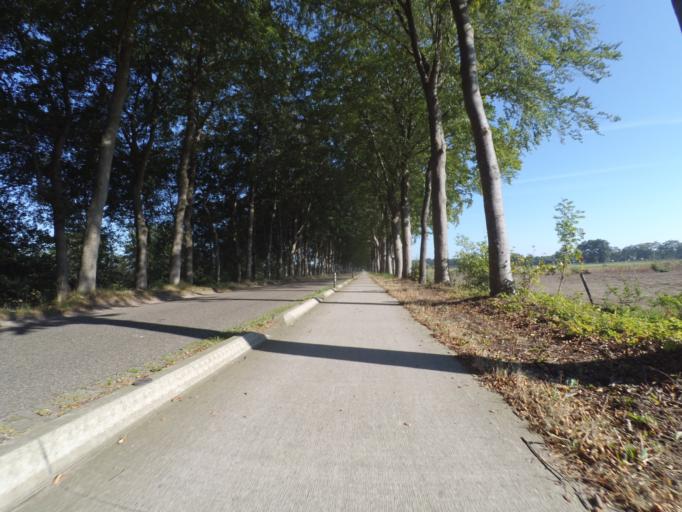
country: NL
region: Gelderland
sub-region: Gemeente Ermelo
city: Horst
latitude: 52.2751
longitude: 5.5689
